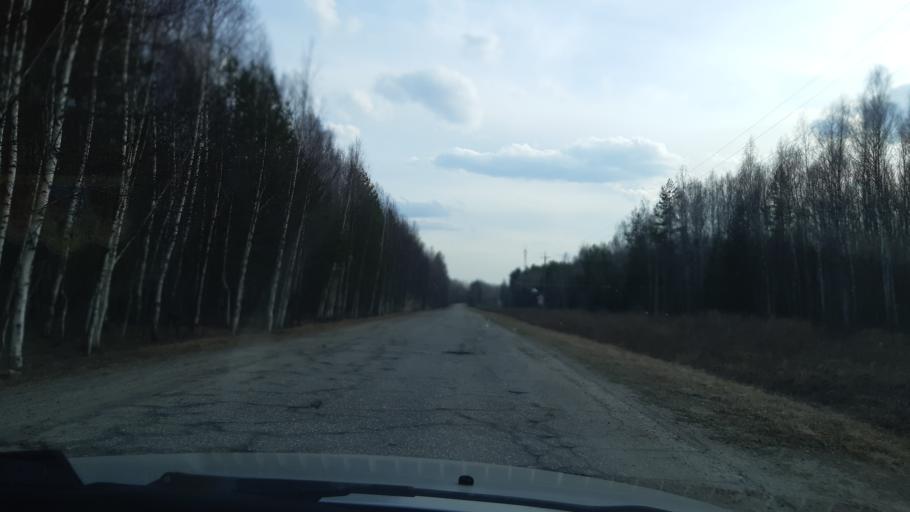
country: RU
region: Vladimir
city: Nikologory
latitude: 56.1131
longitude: 41.9841
